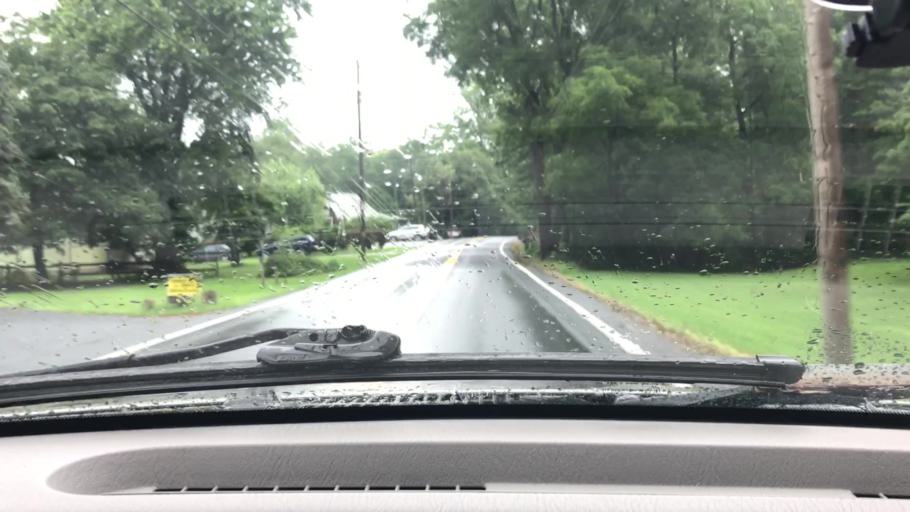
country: US
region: Pennsylvania
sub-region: Lancaster County
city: Elizabethtown
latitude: 40.2133
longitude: -76.6243
